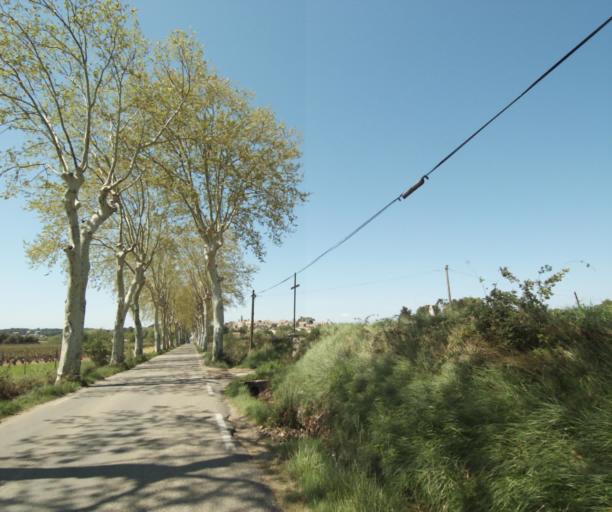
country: FR
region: Languedoc-Roussillon
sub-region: Departement de l'Herault
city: Saint-Genies-des-Mourgues
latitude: 43.6948
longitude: 4.0449
